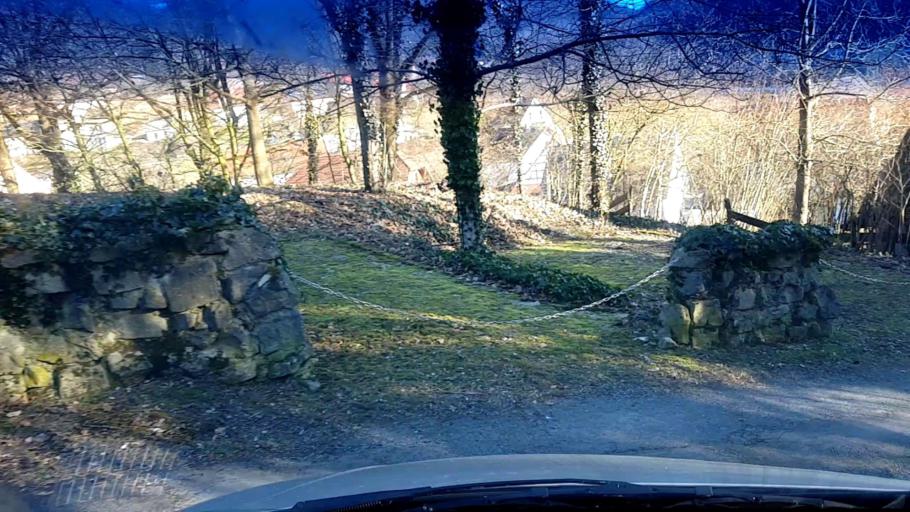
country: DE
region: Bavaria
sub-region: Upper Franconia
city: Poxdorf
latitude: 49.9199
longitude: 11.0756
